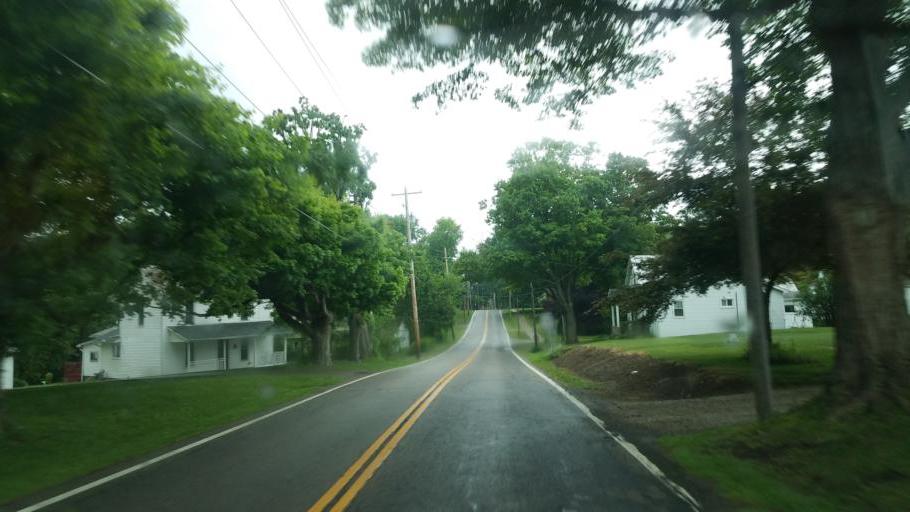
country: US
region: Ohio
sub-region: Knox County
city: Gambier
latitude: 40.3850
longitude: -82.3997
